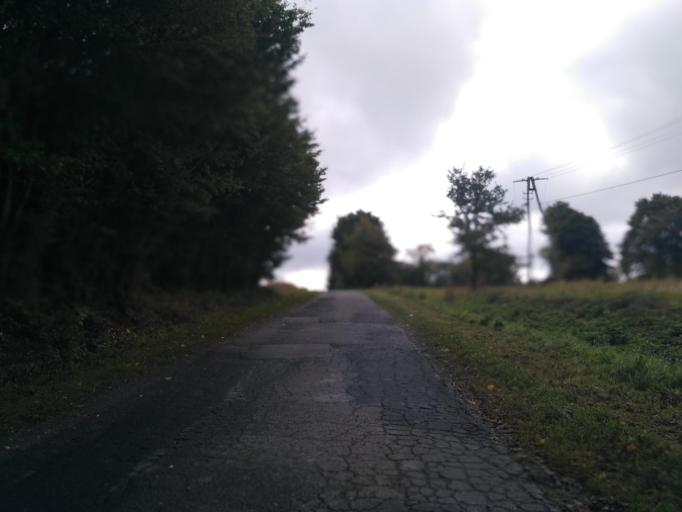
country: PL
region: Subcarpathian Voivodeship
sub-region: Powiat ropczycko-sedziszowski
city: Niedzwiada
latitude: 49.9463
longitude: 21.4619
